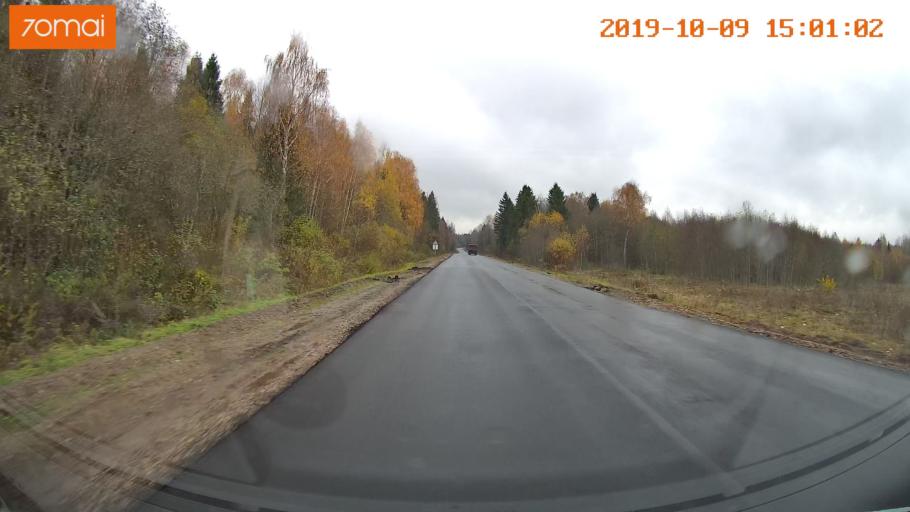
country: RU
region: Kostroma
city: Chistyye Bory
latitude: 58.3016
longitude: 41.6799
